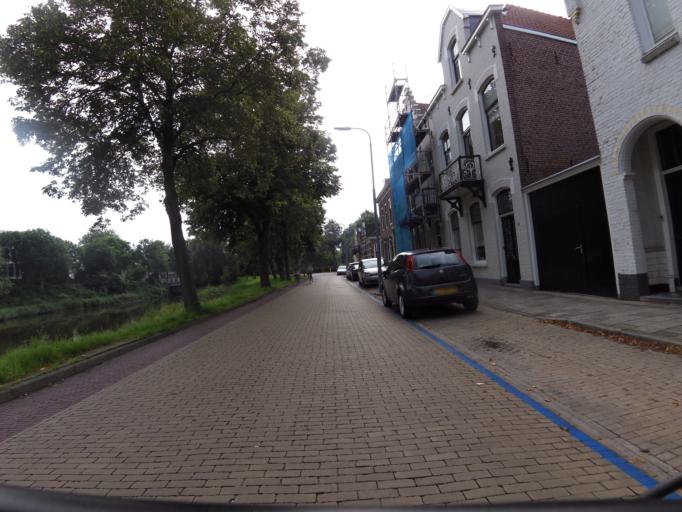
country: NL
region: Zeeland
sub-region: Gemeente Middelburg
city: Middelburg
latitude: 51.5048
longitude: 3.6099
